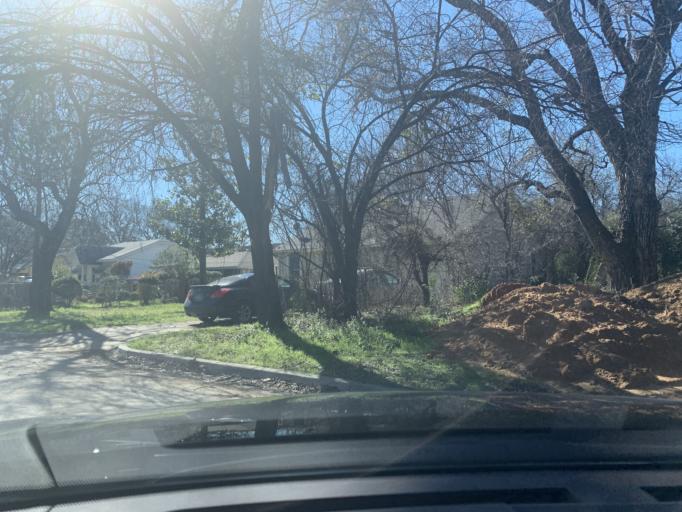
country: US
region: Texas
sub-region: Tarrant County
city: Haltom City
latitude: 32.7684
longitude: -97.2903
